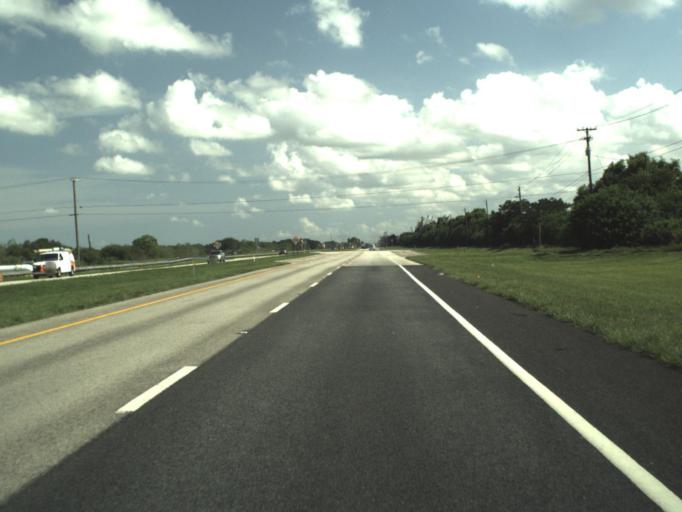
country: US
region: Florida
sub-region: Palm Beach County
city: Villages of Oriole
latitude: 26.4248
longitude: -80.2044
